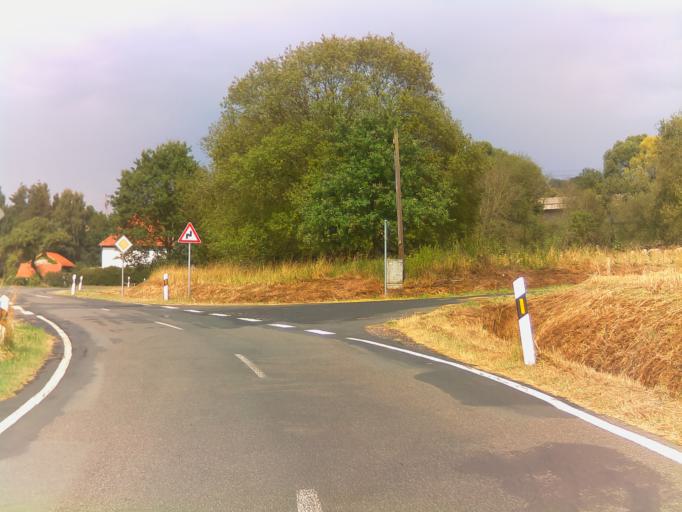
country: DE
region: Hesse
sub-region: Regierungsbezirk Kassel
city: Niederaula
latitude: 50.7720
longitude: 9.5980
